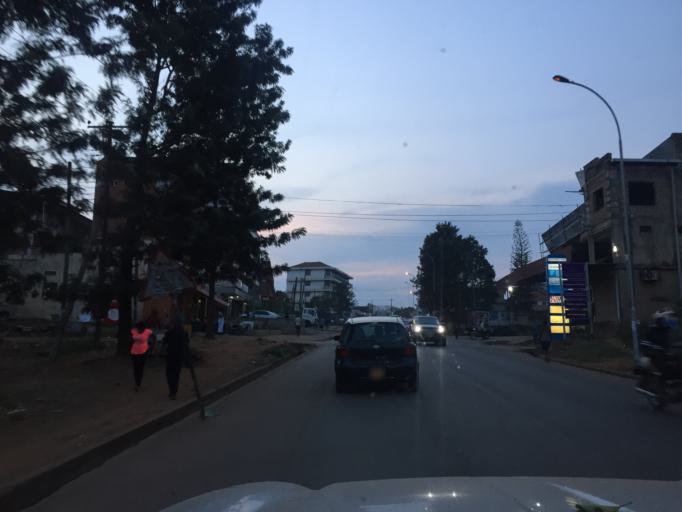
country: UG
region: Central Region
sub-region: Kampala District
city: Kampala
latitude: 0.2835
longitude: 32.6099
